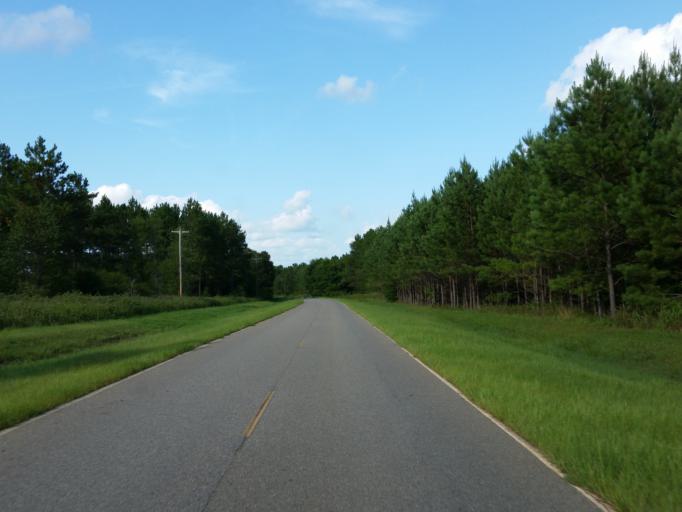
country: US
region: Georgia
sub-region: Lee County
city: Leesburg
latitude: 31.9062
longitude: -84.0327
